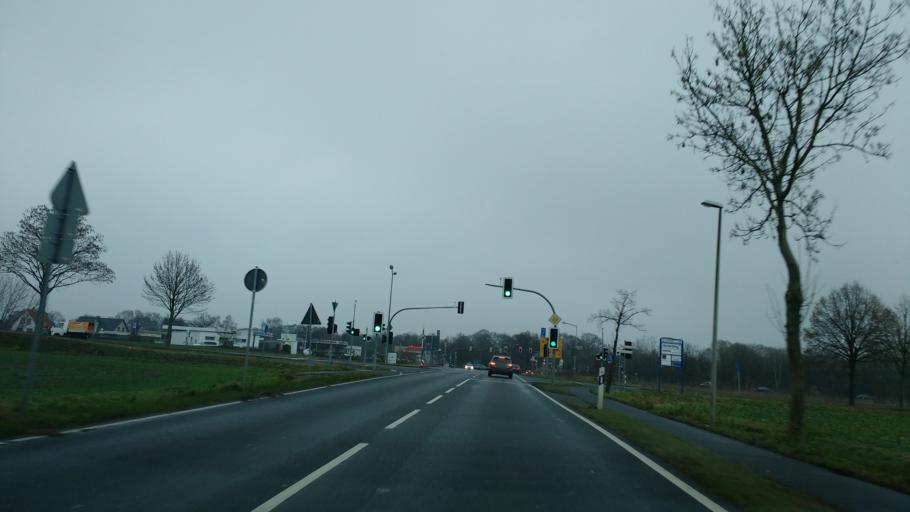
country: DE
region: Lower Saxony
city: Garbsen-Mitte
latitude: 52.4375
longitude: 9.5880
